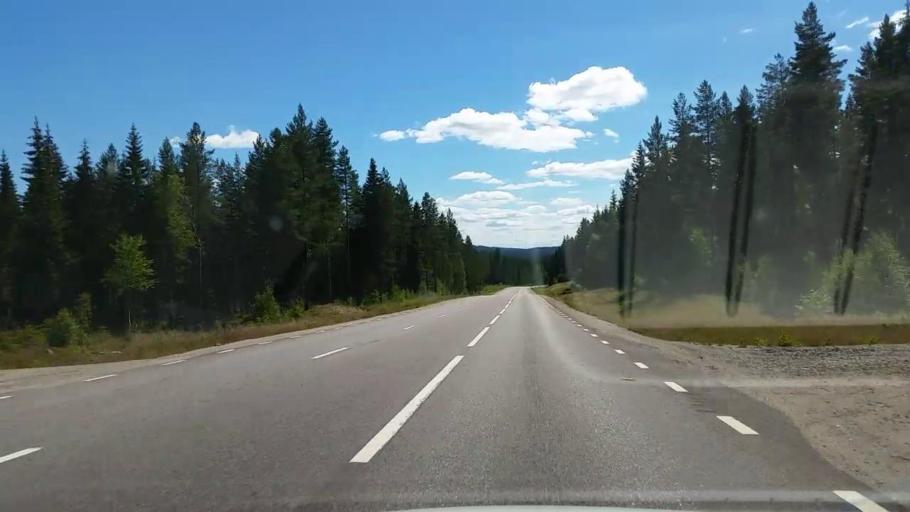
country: SE
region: Gaevleborg
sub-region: Bollnas Kommun
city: Vittsjo
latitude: 61.0541
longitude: 15.8020
